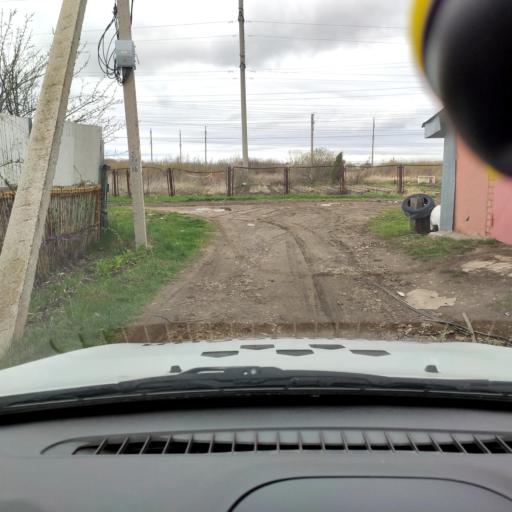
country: RU
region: Samara
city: Tol'yatti
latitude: 53.5868
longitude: 49.3167
